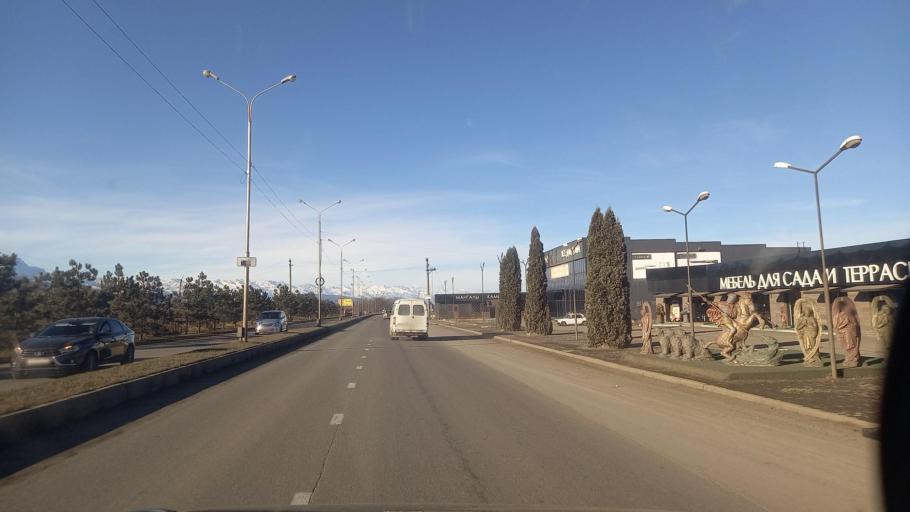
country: RU
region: North Ossetia
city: Vladikavkaz
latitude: 43.0254
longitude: 44.6318
